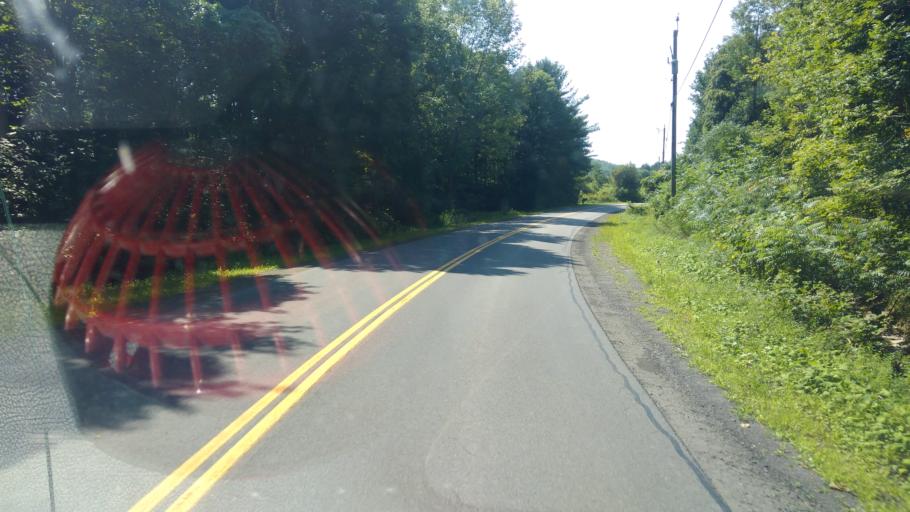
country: US
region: New York
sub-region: Allegany County
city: Belmont
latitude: 42.2704
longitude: -77.9923
